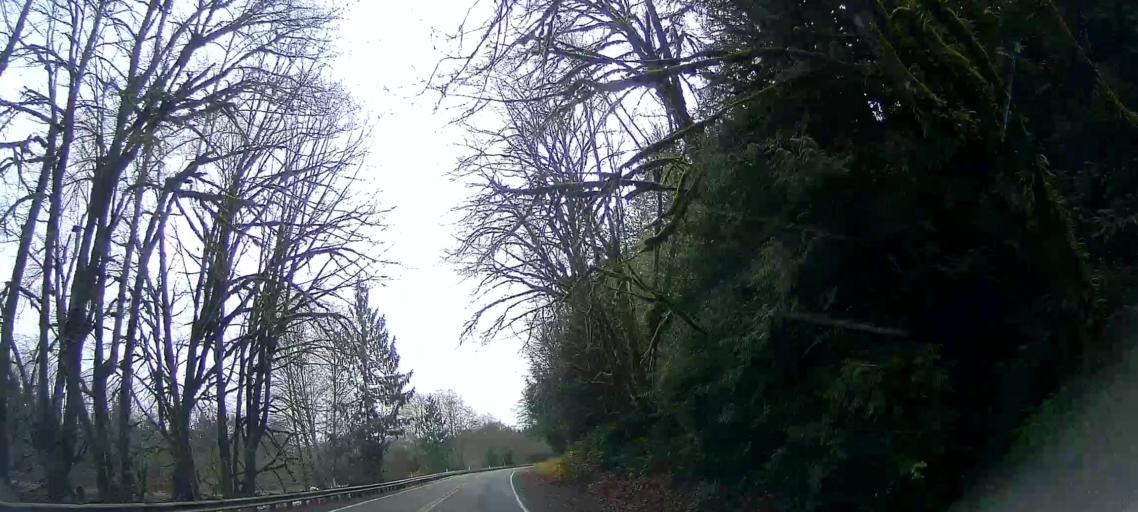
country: US
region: Washington
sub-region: Snohomish County
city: Darrington
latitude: 48.5175
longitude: -121.8604
